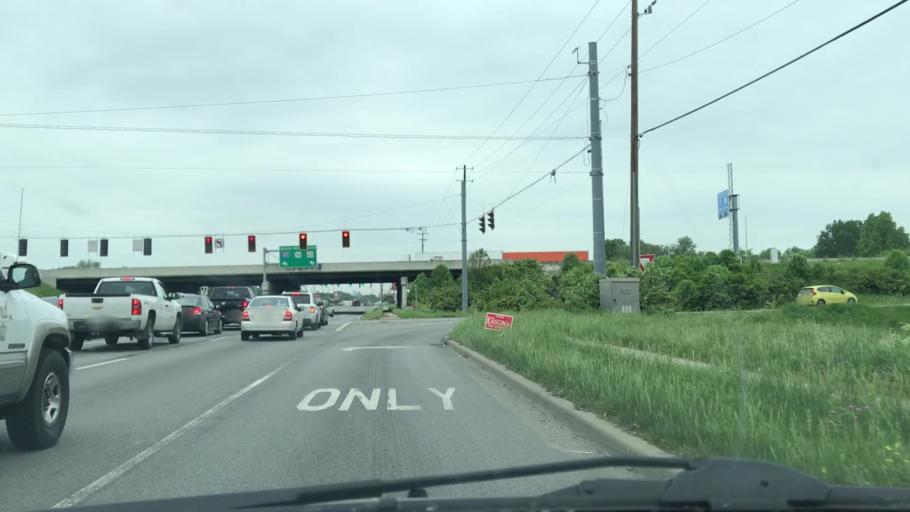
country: US
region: Indiana
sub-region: Marion County
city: Lawrence
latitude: 39.8330
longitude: -86.0344
